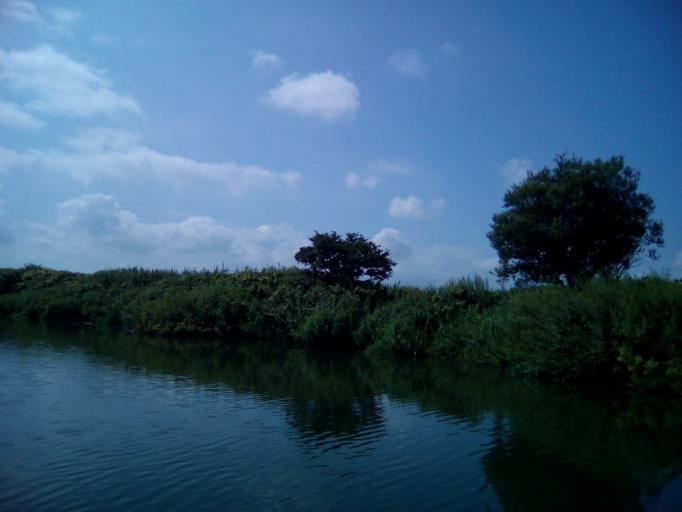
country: JP
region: Hokkaido
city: Tobetsu
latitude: 43.1471
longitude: 141.4508
